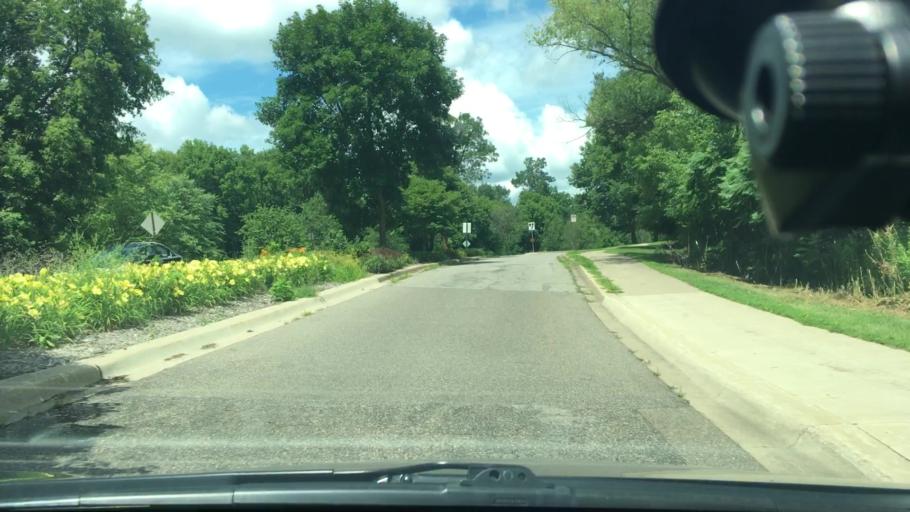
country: US
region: Minnesota
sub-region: Hennepin County
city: Plymouth
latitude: 45.0003
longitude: -93.4309
